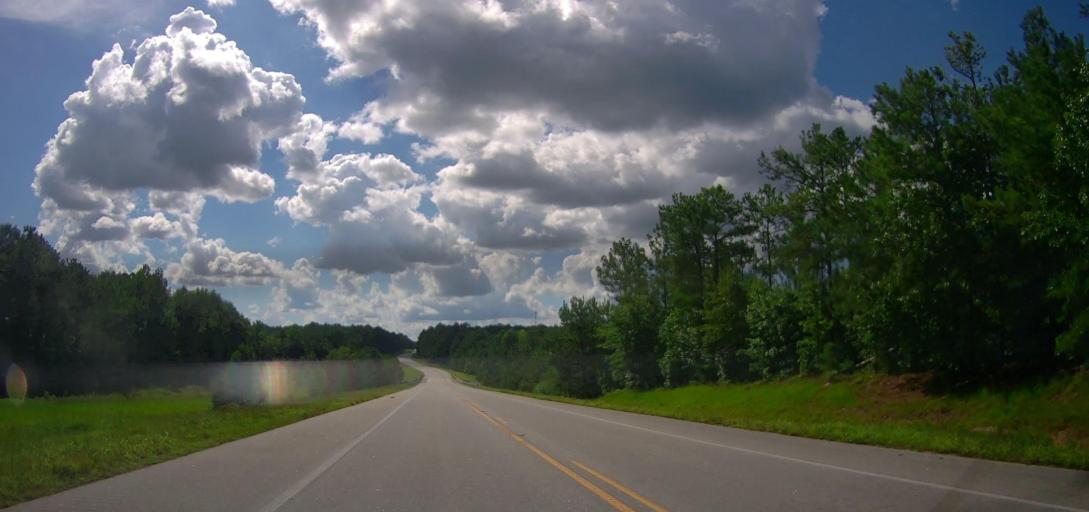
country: US
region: Alabama
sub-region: Lee County
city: Auburn
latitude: 32.4391
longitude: -85.4878
